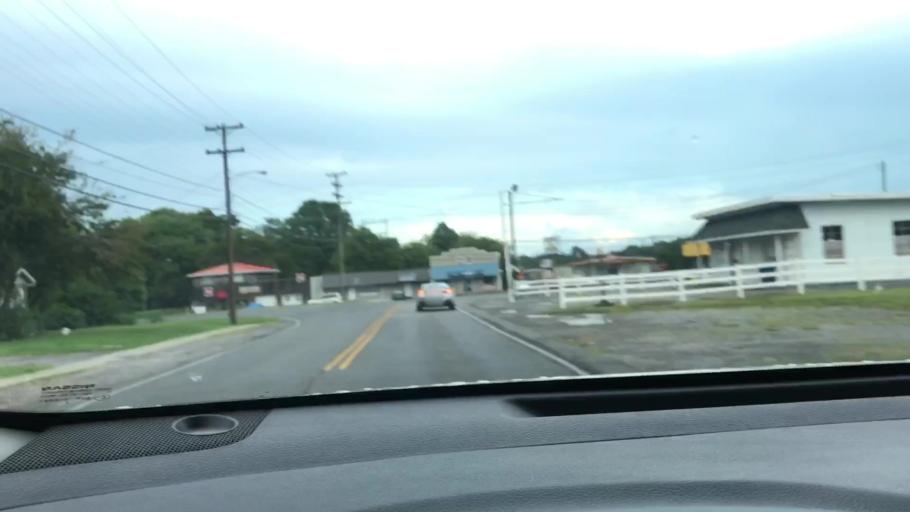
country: US
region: Kentucky
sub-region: Calloway County
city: Murray
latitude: 36.6027
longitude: -88.3038
